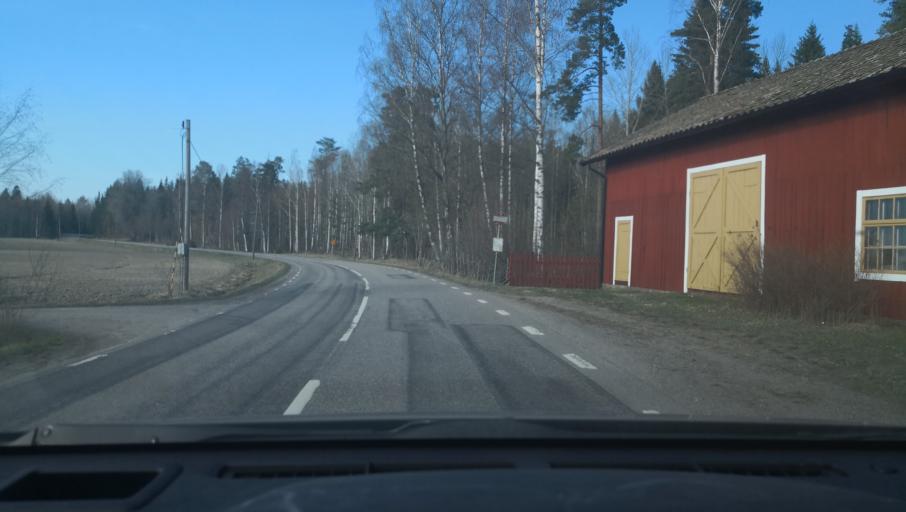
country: SE
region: Uppsala
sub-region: Heby Kommun
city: Heby
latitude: 59.9651
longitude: 16.8944
